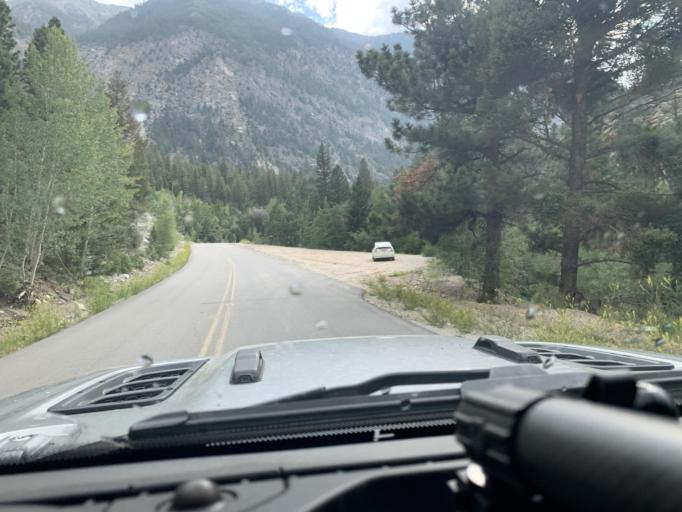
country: US
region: Colorado
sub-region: Chaffee County
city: Buena Vista
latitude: 38.7100
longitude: -106.2394
